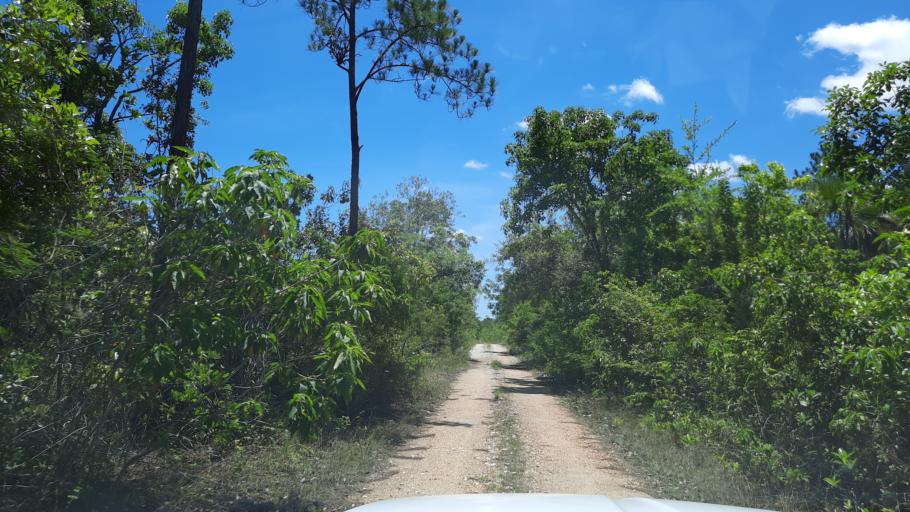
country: BZ
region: Cayo
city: Belmopan
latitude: 17.3596
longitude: -88.5330
